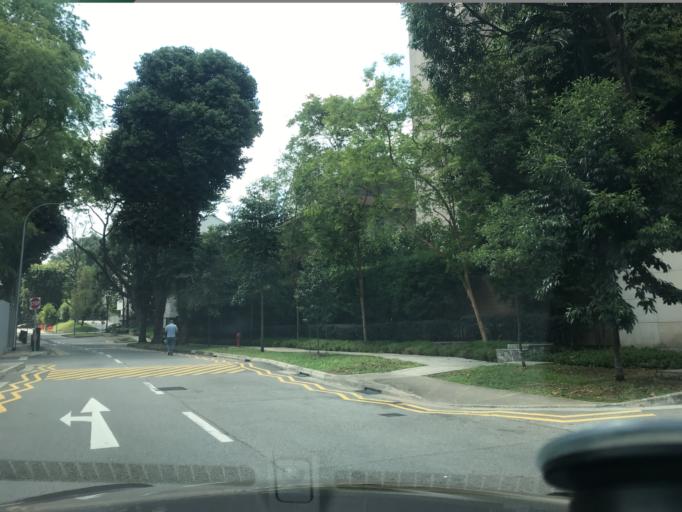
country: SG
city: Singapore
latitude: 1.3059
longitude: 103.8231
